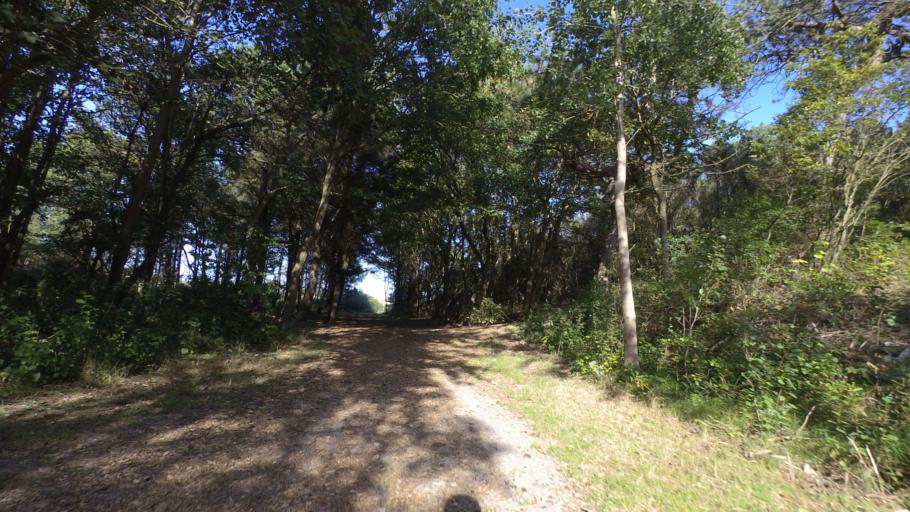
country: NL
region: Friesland
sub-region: Gemeente Ameland
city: Nes
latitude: 53.4545
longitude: 5.7653
